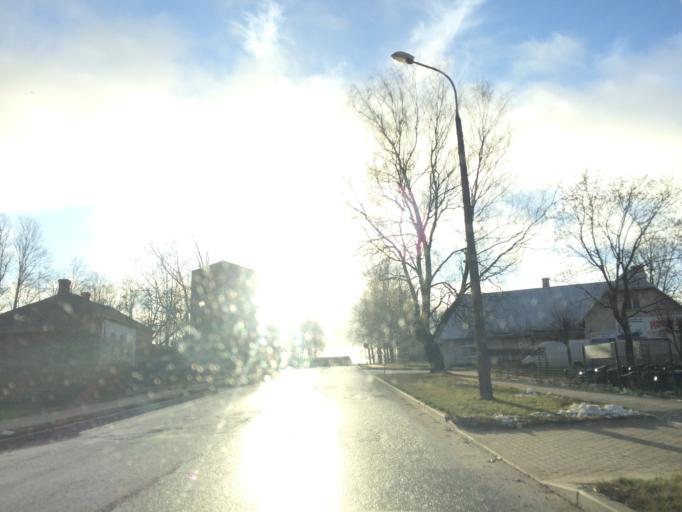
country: LV
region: Rezekne
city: Rezekne
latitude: 56.5116
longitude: 27.3251
